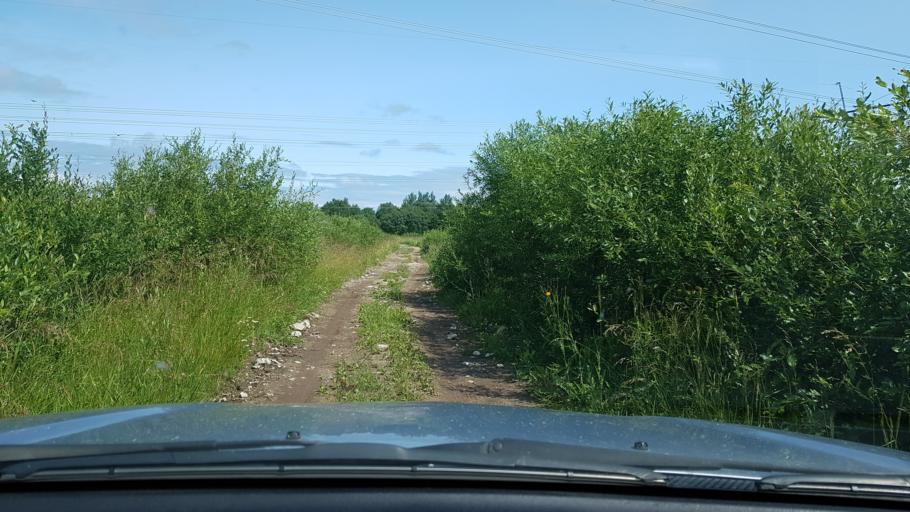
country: EE
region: Ida-Virumaa
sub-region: Sillamaee linn
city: Sillamae
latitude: 59.3608
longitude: 27.7844
